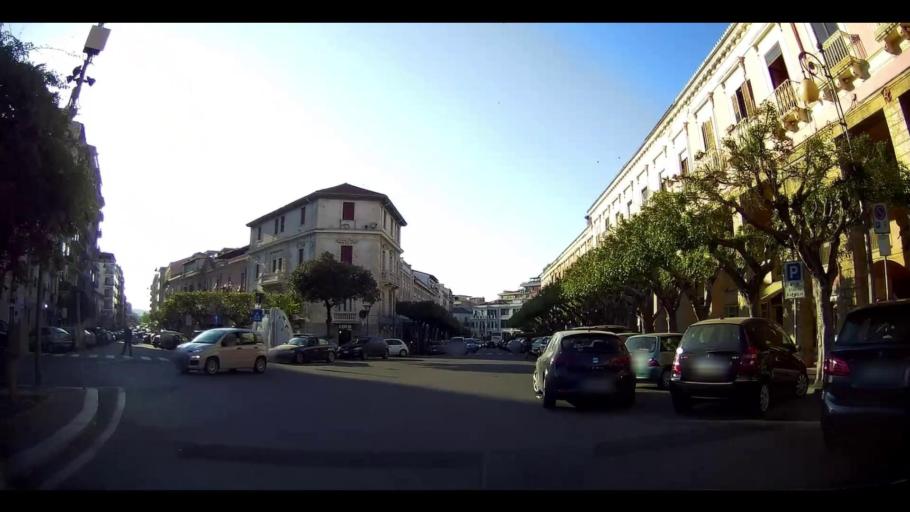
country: IT
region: Calabria
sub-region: Provincia di Crotone
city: Crotone
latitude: 39.0809
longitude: 17.1270
